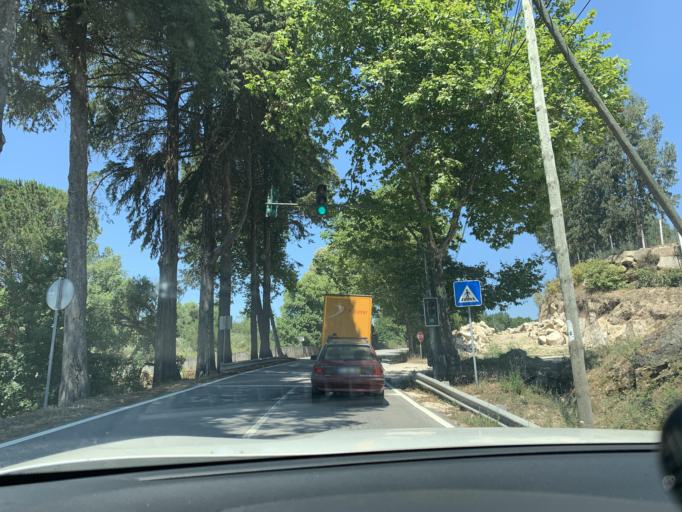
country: PT
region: Viseu
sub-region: Mangualde
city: Mangualde
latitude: 40.5948
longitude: -7.7987
